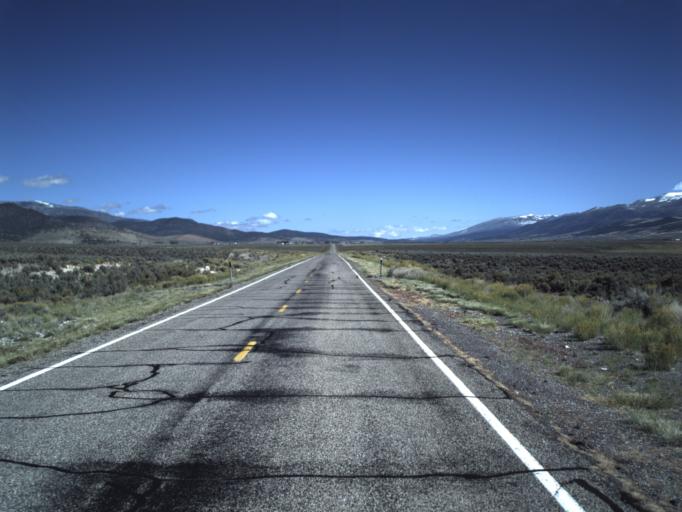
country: US
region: Utah
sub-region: Wayne County
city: Loa
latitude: 38.3860
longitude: -111.9341
